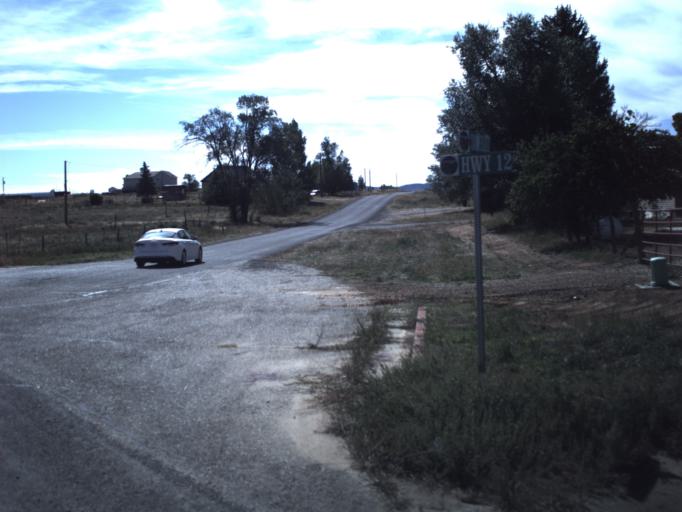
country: US
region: Utah
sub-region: Wayne County
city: Loa
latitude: 37.7695
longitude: -111.5946
